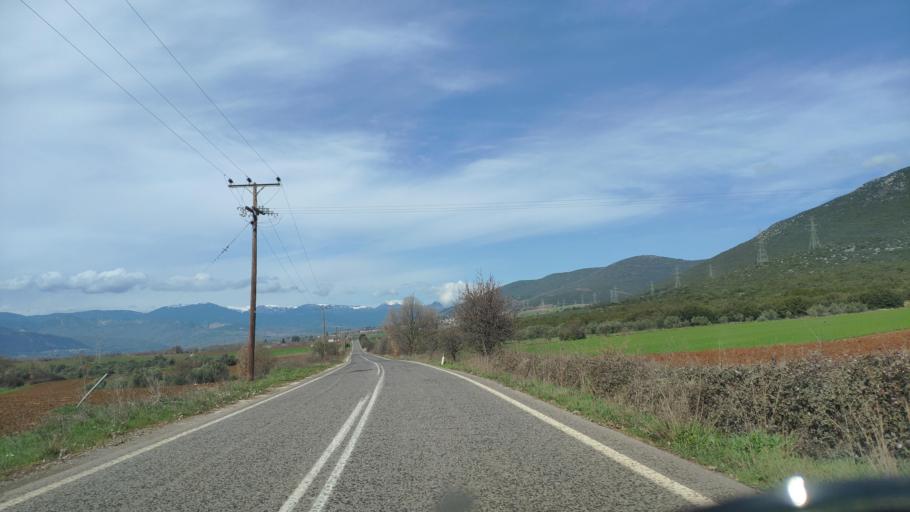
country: GR
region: Central Greece
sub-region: Nomos Fthiotidos
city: Amfikleia
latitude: 38.6985
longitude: 22.5185
